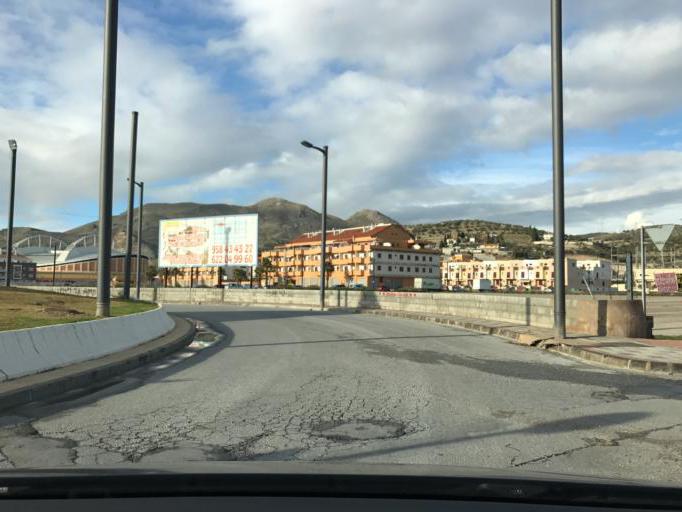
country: ES
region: Andalusia
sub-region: Provincia de Granada
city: Atarfe
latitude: 37.2217
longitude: -3.6980
